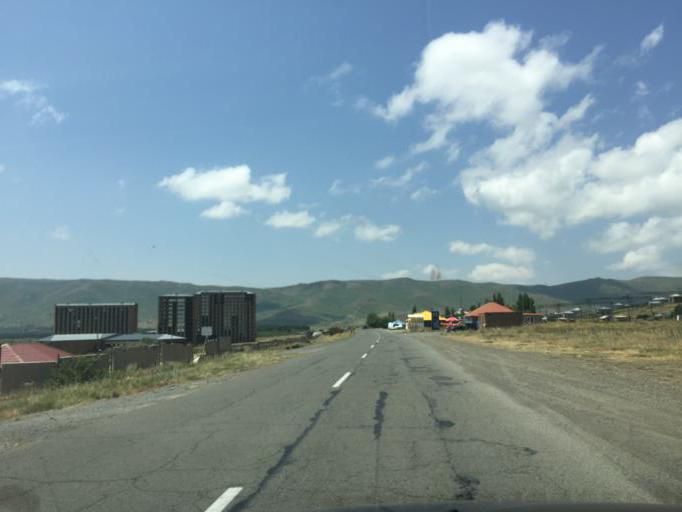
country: AM
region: Geghark'unik'i Marz
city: Tsovagyugh
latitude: 40.6290
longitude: 44.9764
